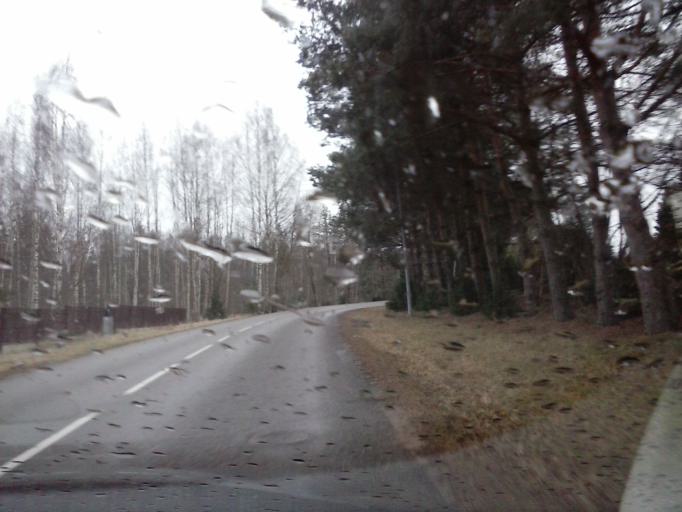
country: EE
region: Polvamaa
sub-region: Polva linn
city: Polva
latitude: 58.0536
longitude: 27.0688
